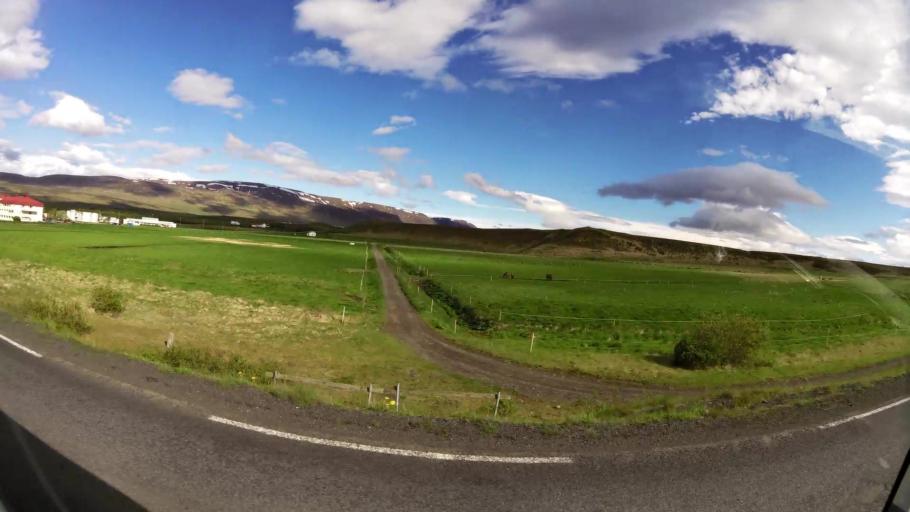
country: IS
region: Northwest
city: Saudarkrokur
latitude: 65.6550
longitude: -20.2859
